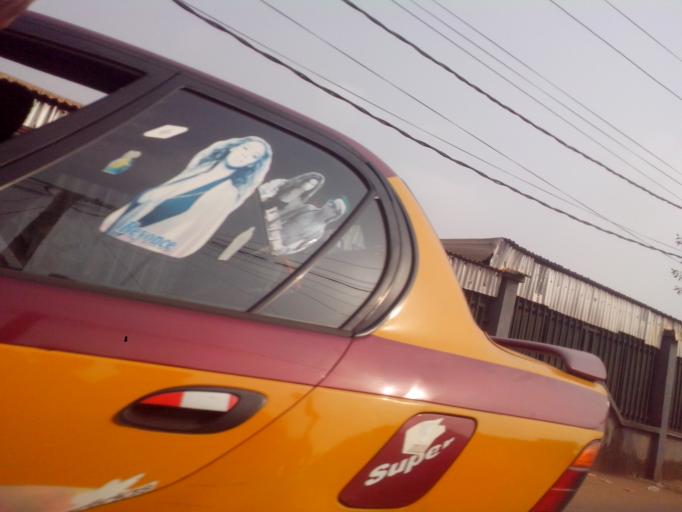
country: CM
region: Centre
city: Yaounde
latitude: 3.8504
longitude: 11.4938
